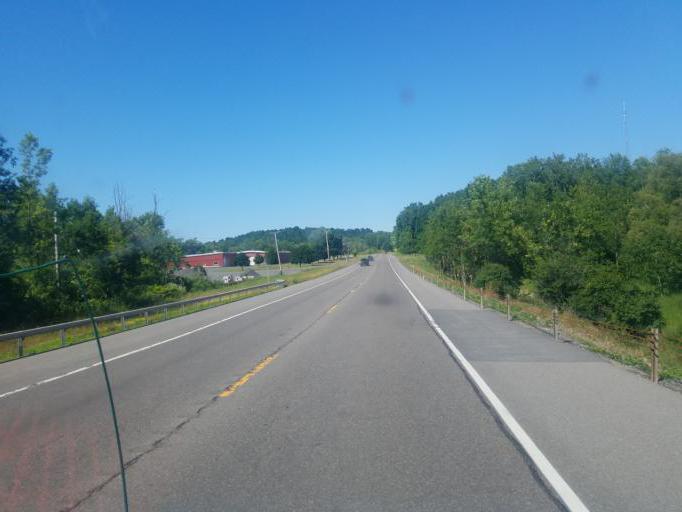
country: US
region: New York
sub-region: Wayne County
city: Lyons
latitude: 43.0642
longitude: -77.0402
